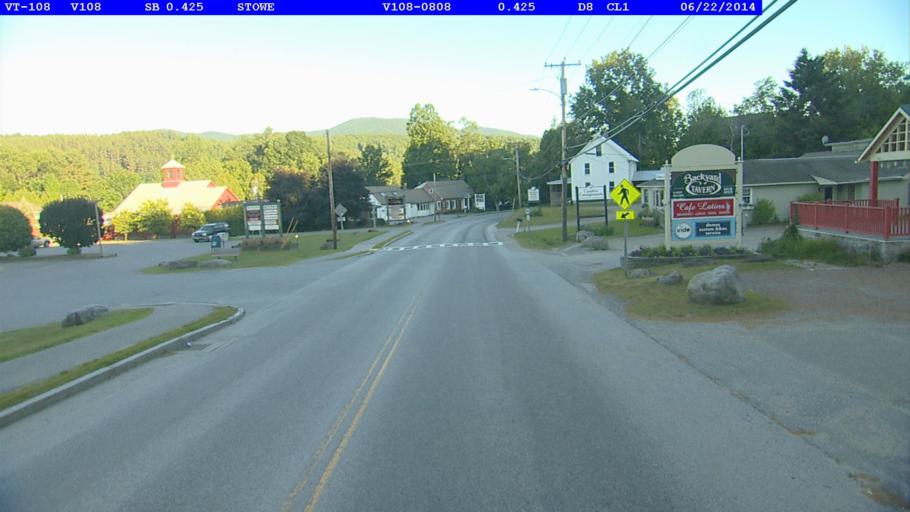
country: US
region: Vermont
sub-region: Lamoille County
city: Morristown
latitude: 44.4710
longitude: -72.6879
